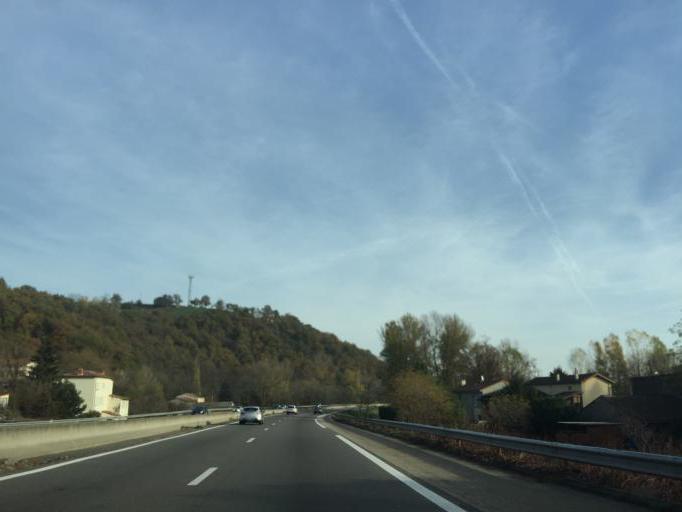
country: FR
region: Rhone-Alpes
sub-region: Departement du Rhone
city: Echalas
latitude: 45.5654
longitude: 4.7039
